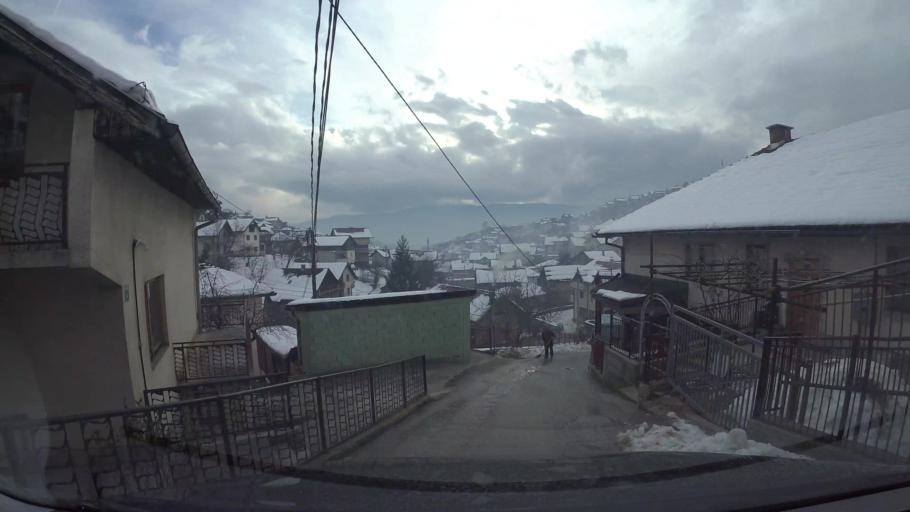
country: BA
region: Federation of Bosnia and Herzegovina
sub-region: Kanton Sarajevo
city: Sarajevo
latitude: 43.8603
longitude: 18.3479
